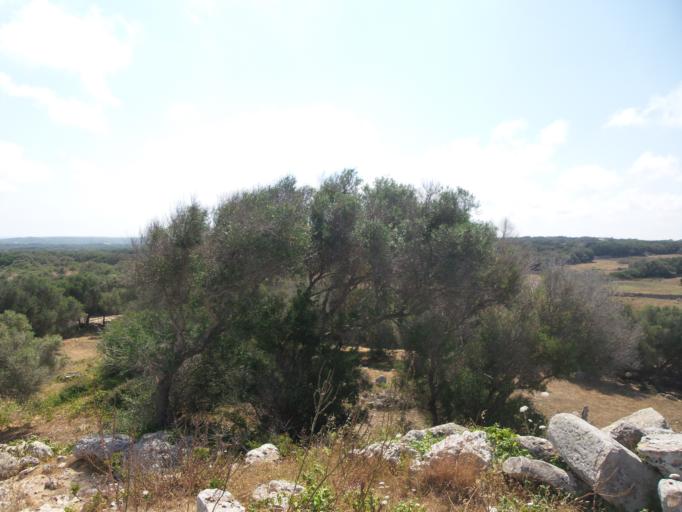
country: ES
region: Balearic Islands
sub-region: Illes Balears
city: Mao
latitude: 39.8929
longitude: 4.2154
